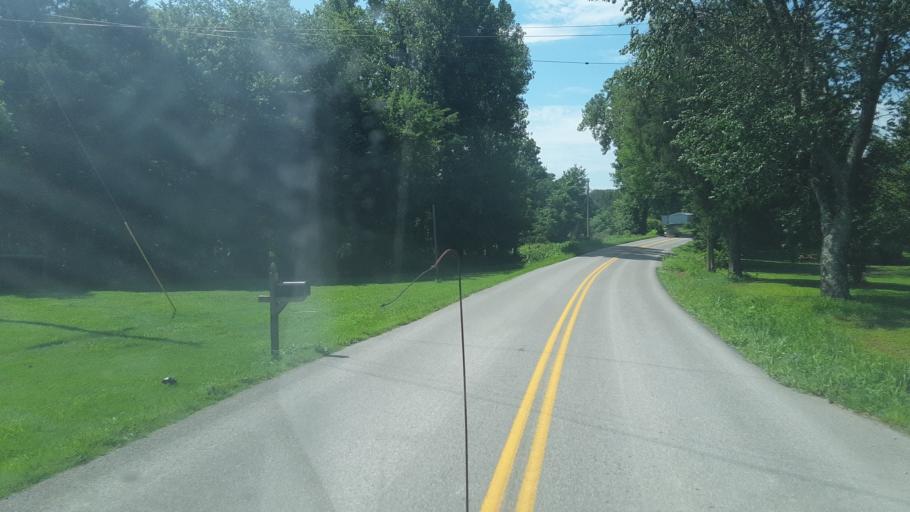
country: US
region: Kentucky
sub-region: Todd County
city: Elkton
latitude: 36.8391
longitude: -87.3007
